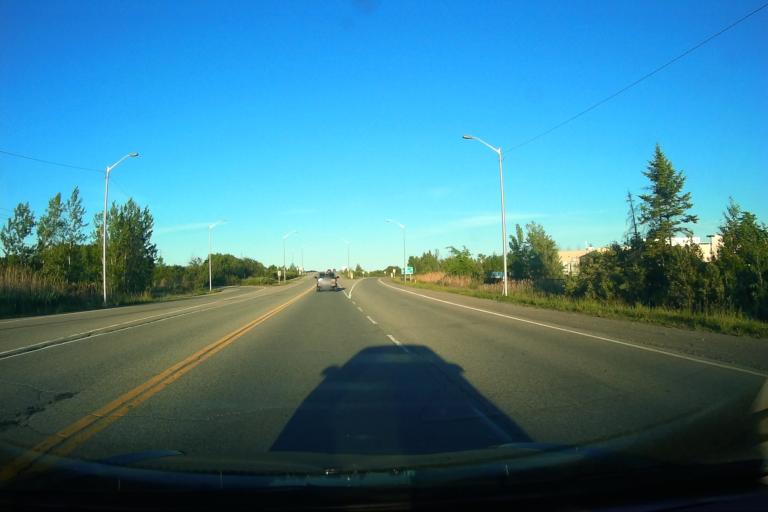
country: CA
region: Ontario
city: Prescott
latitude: 45.0304
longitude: -75.6301
